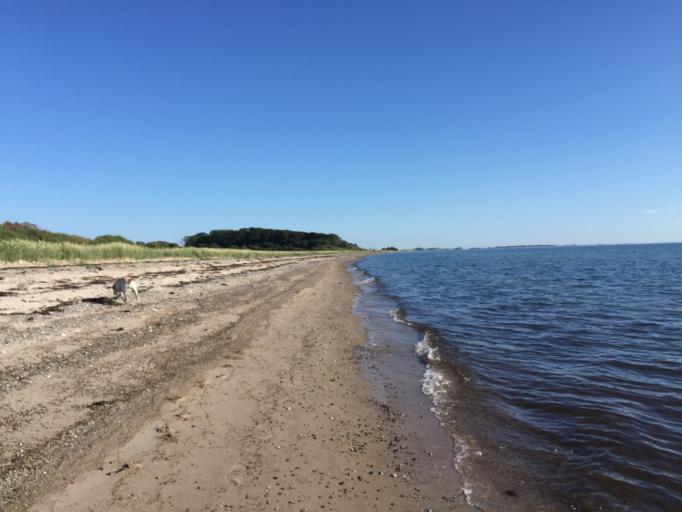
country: DK
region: Zealand
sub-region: Slagelse Kommune
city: Korsor
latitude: 55.2285
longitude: 11.1713
